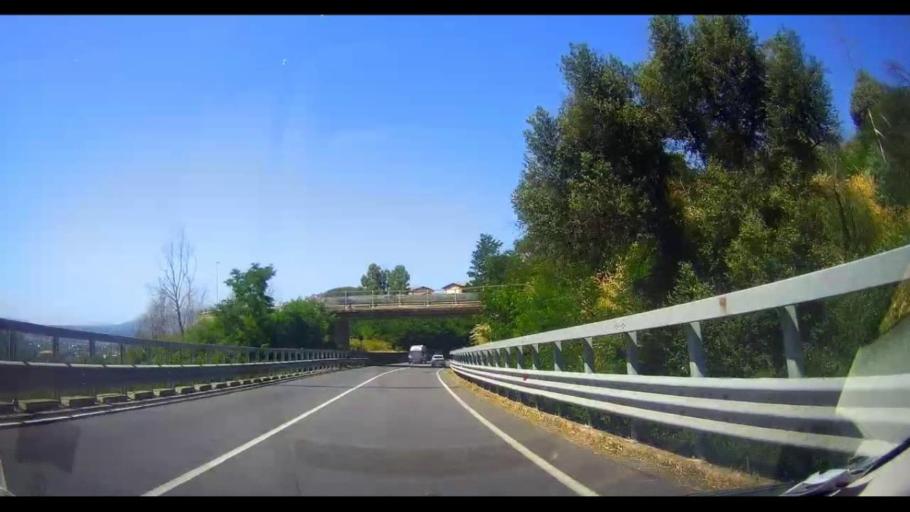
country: IT
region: Calabria
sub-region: Provincia di Cosenza
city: Rovito
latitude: 39.2976
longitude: 16.3083
